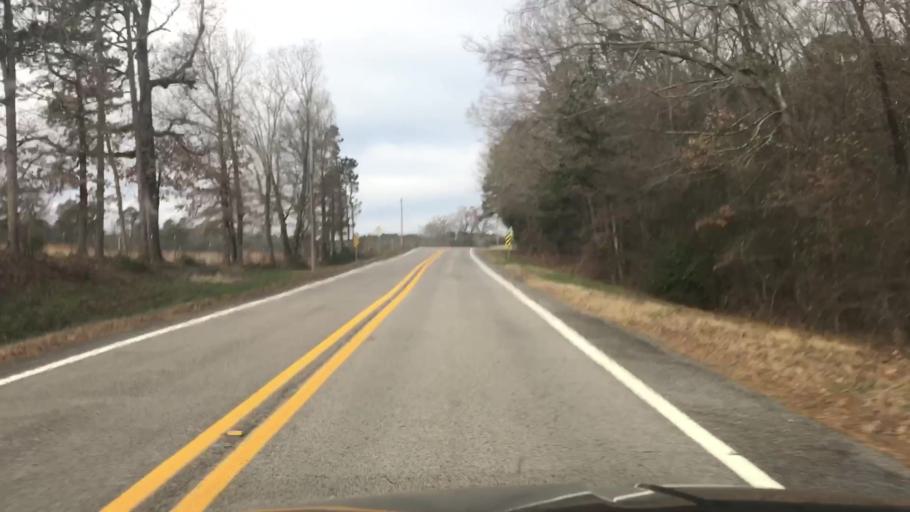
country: US
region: Arkansas
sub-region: Montgomery County
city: Mount Ida
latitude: 34.6606
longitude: -93.7676
